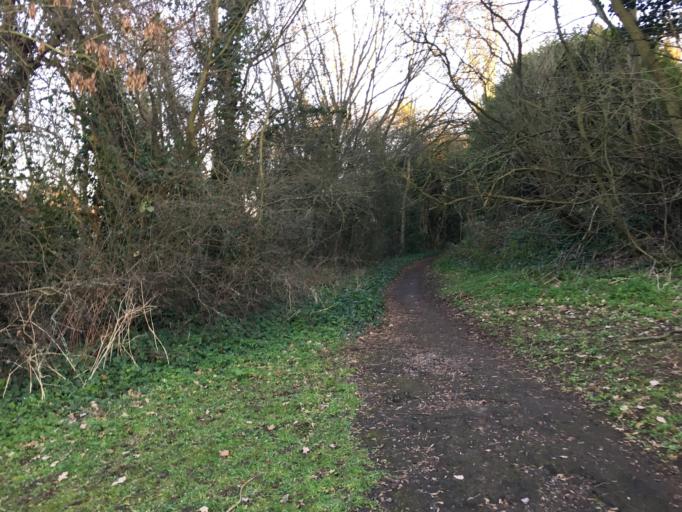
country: GB
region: England
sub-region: Greater London
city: Hendon
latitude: 51.5880
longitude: -0.1945
